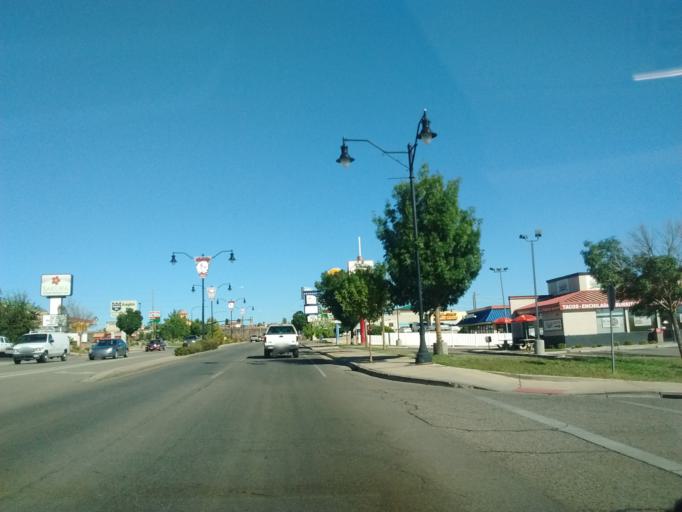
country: US
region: Utah
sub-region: Washington County
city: Saint George
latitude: 37.1097
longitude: -113.5642
